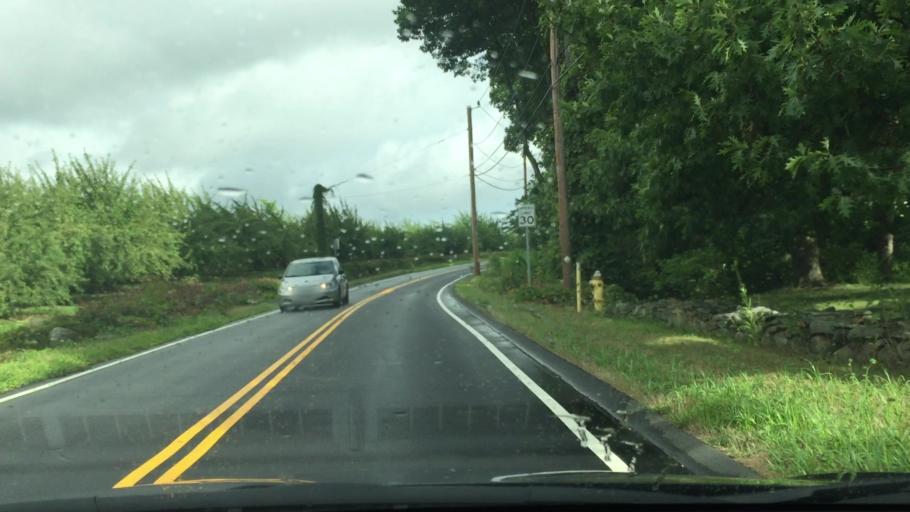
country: US
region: Massachusetts
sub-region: Middlesex County
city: Littleton Common
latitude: 42.5156
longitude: -71.4546
